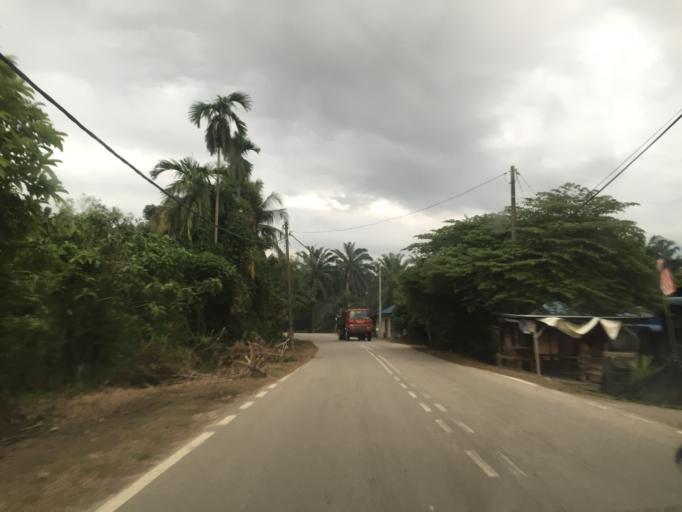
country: MY
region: Penang
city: Tasek Glugor
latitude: 5.5430
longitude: 100.5250
